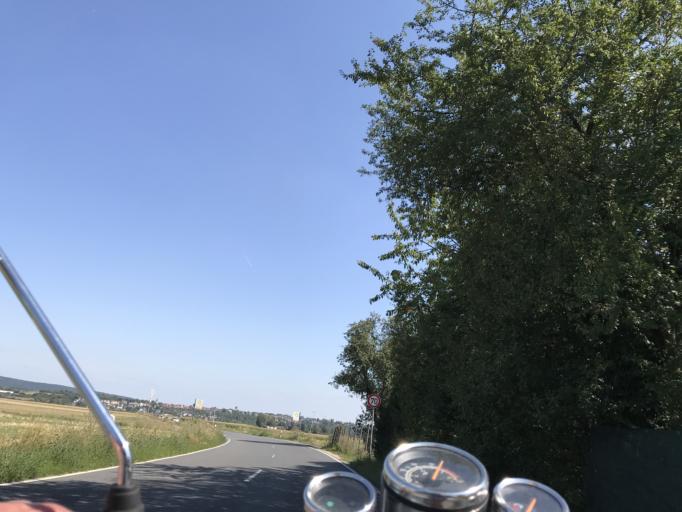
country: DE
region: Hesse
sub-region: Regierungsbezirk Darmstadt
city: Wiesbaden
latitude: 50.0818
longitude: 8.2974
